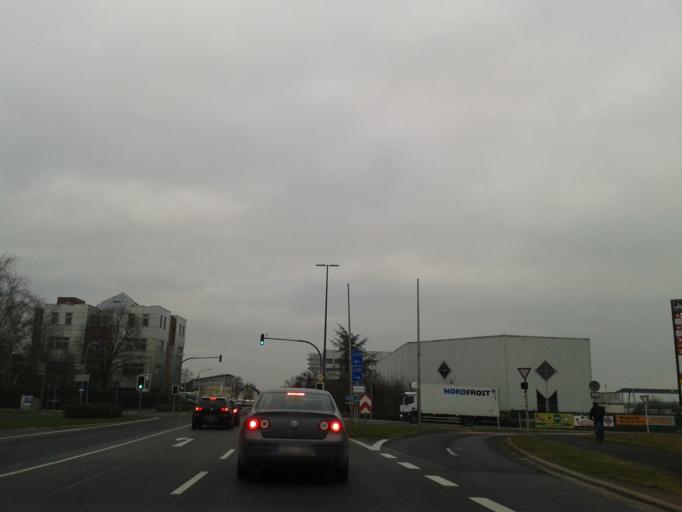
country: DE
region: Bavaria
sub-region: Upper Franconia
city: Hallstadt
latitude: 49.9140
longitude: 10.8777
